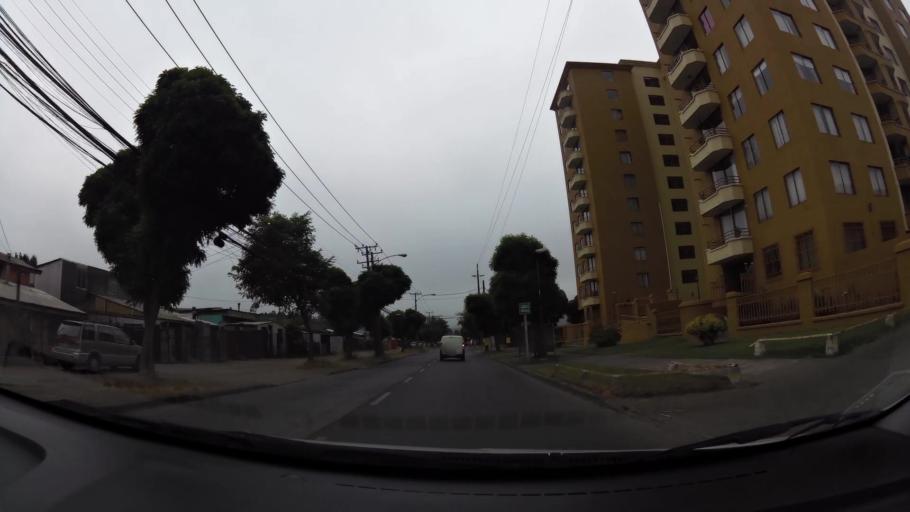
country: CL
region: Biobio
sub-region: Provincia de Concepcion
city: Concepcion
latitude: -36.8163
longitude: -73.0442
